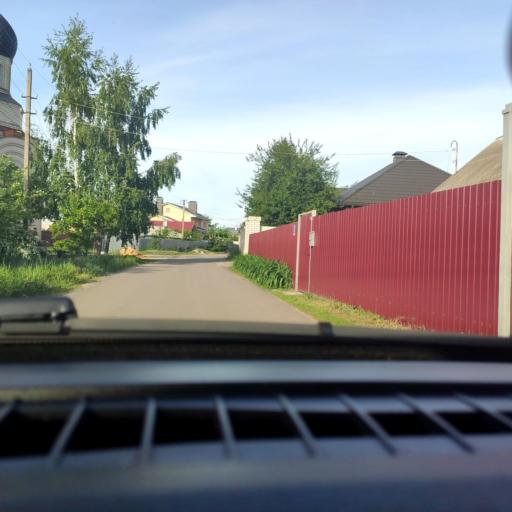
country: RU
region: Voronezj
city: Podgornoye
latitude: 51.7898
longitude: 39.1384
